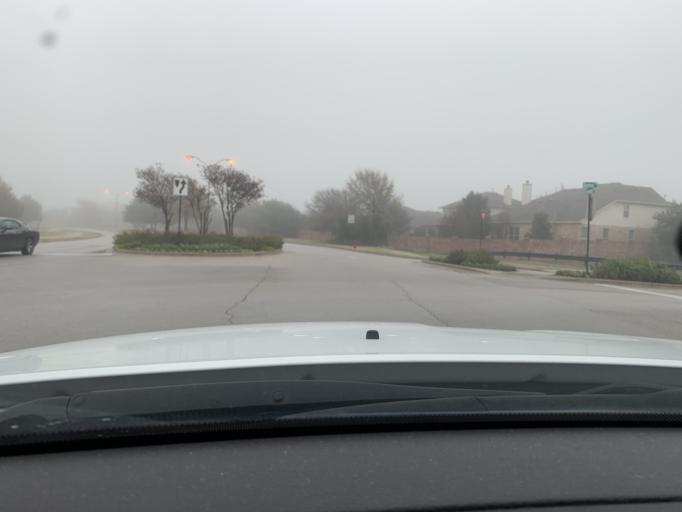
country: US
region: Texas
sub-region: Williamson County
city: Round Rock
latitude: 30.5639
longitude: -97.6807
